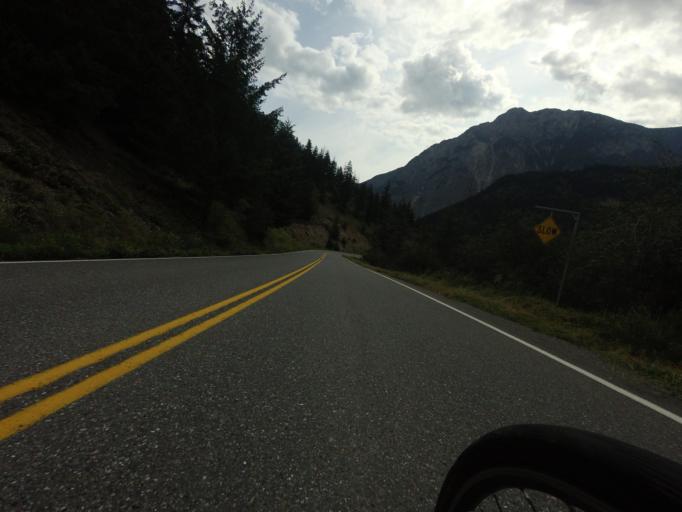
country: CA
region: British Columbia
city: Lillooet
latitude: 50.6529
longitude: -122.0066
